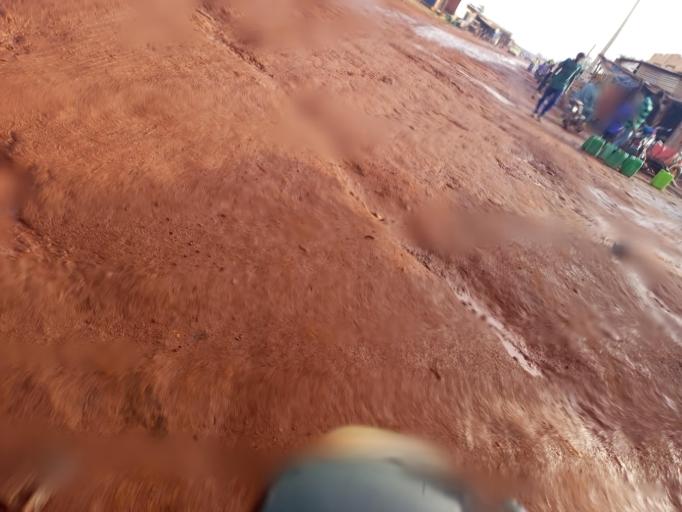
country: ML
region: Bamako
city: Bamako
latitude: 12.5301
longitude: -7.9947
